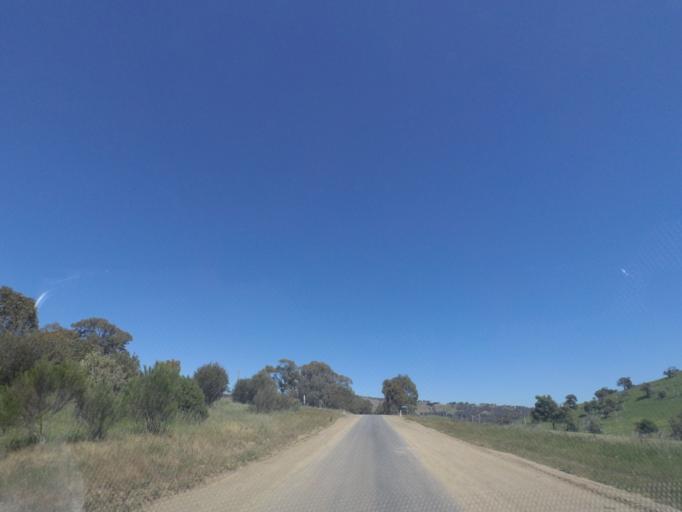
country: AU
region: Victoria
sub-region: Whittlesea
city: Whittlesea
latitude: -37.2882
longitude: 144.9955
